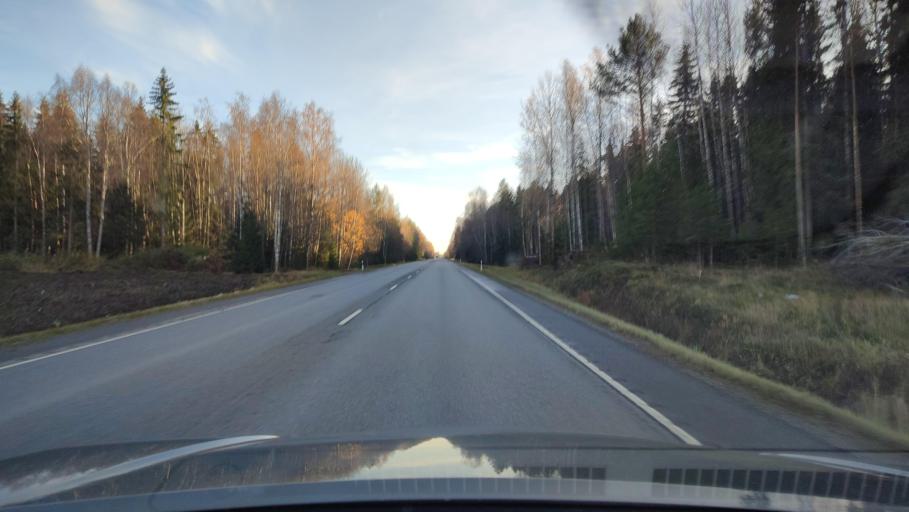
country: FI
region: Ostrobothnia
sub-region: Vaasa
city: Ristinummi
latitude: 63.0053
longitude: 21.7632
